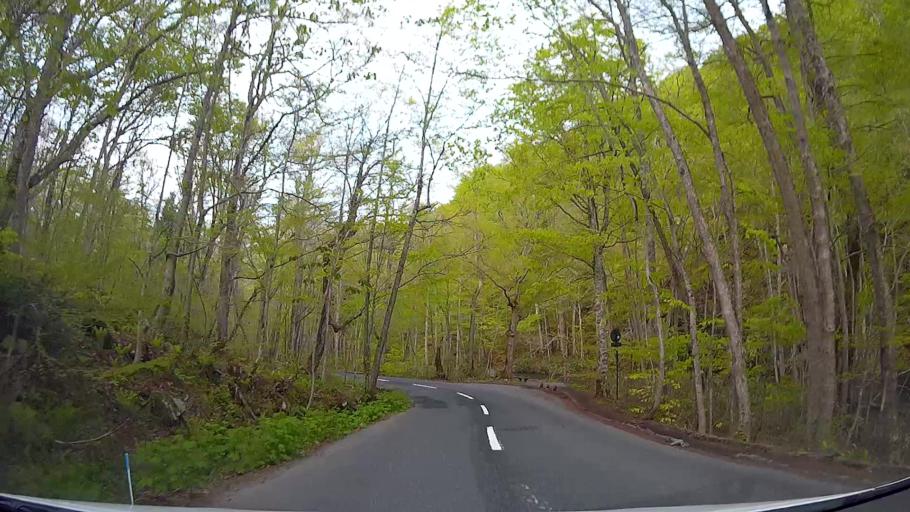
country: JP
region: Aomori
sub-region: Aomori Shi
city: Furudate
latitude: 40.5229
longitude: 140.9733
